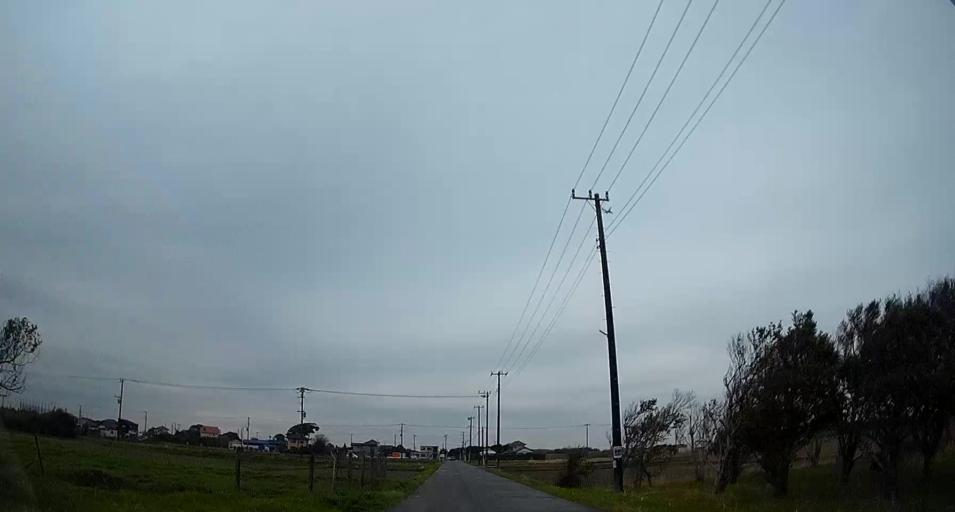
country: JP
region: Chiba
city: Kisarazu
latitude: 35.4134
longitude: 139.9119
